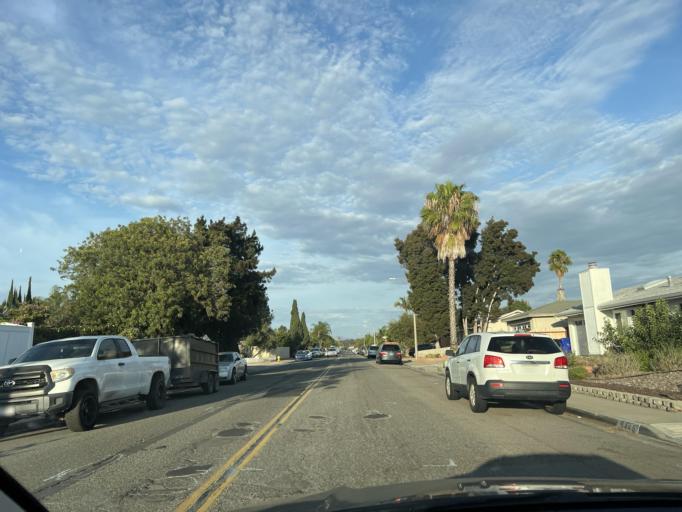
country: US
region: California
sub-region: San Diego County
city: Fairbanks Ranch
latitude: 32.9022
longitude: -117.1418
